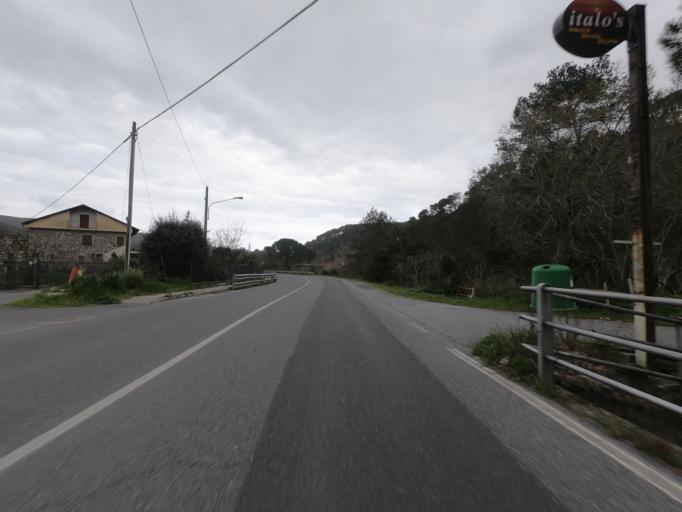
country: IT
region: Liguria
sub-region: Provincia di Imperia
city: Villa Faraldi
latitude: 43.9946
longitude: 8.1150
